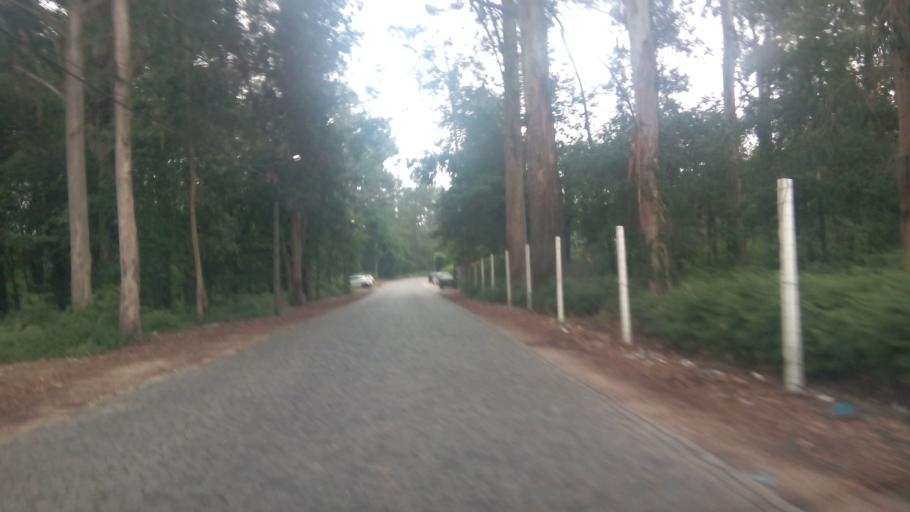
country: PT
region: Porto
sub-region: Paredes
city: Casteloes de Cepeda
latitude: 41.1877
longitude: -8.3450
